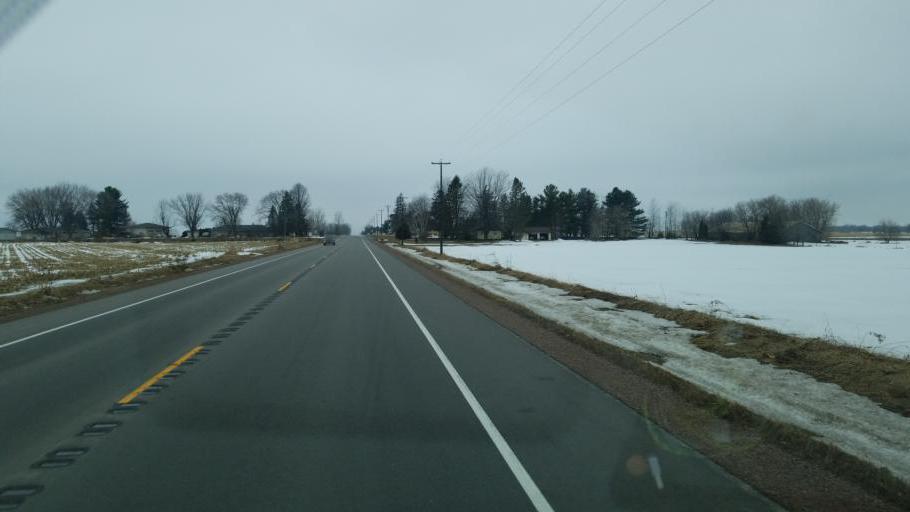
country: US
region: Wisconsin
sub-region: Marathon County
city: Spencer
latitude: 44.6563
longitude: -90.2762
